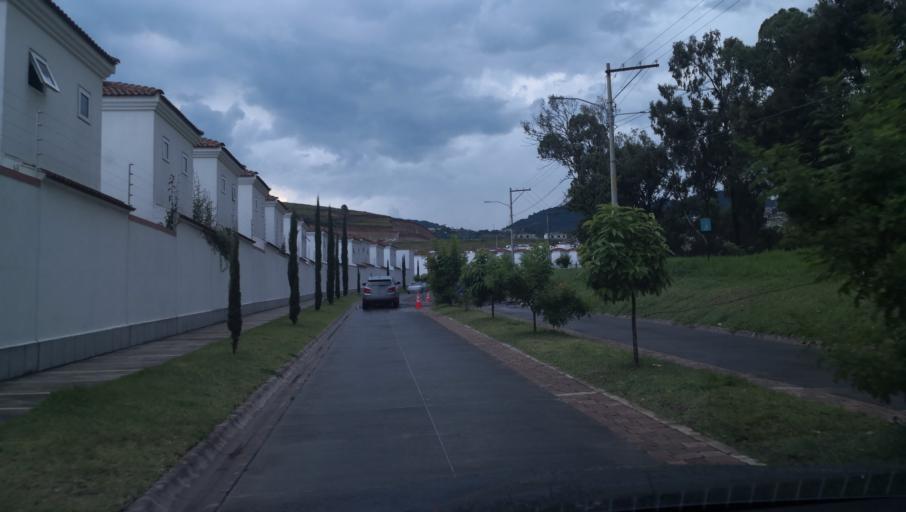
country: GT
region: Guatemala
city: Villa Nueva
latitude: 14.5623
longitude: -90.5971
